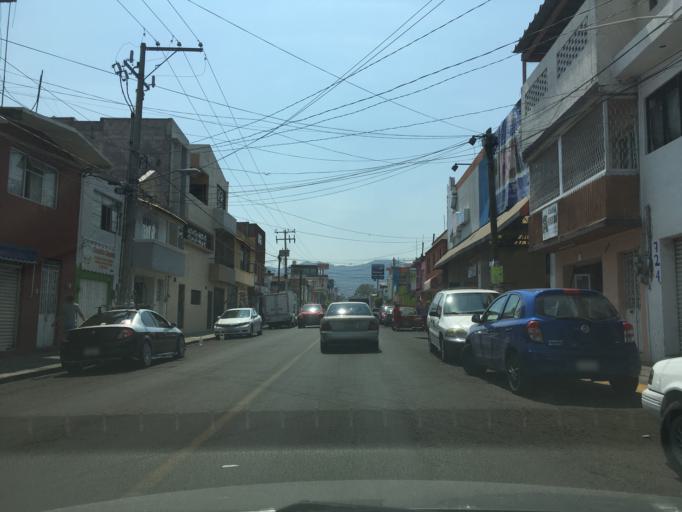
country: MX
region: Michoacan
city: Morelia
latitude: 19.7027
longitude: -101.1734
